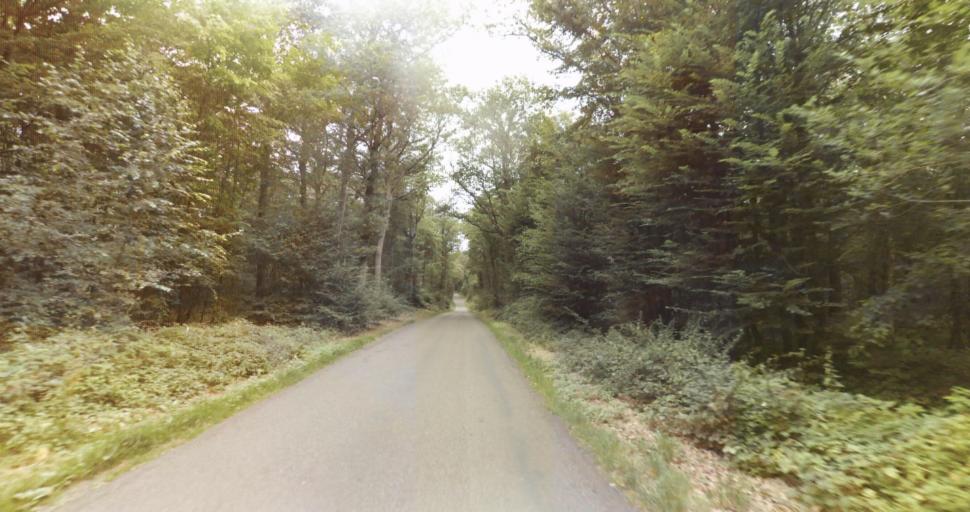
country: FR
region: Haute-Normandie
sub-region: Departement de l'Eure
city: Marcilly-sur-Eure
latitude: 48.8691
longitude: 1.3376
